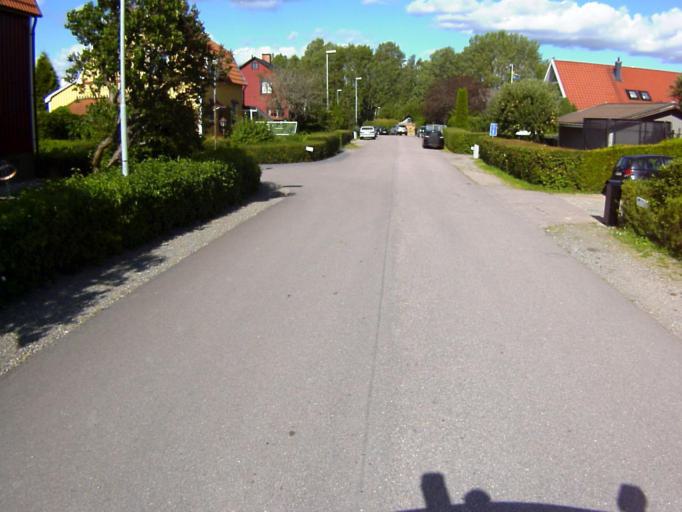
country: SE
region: Soedermanland
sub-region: Eskilstuna Kommun
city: Eskilstuna
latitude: 59.3752
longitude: 16.4828
